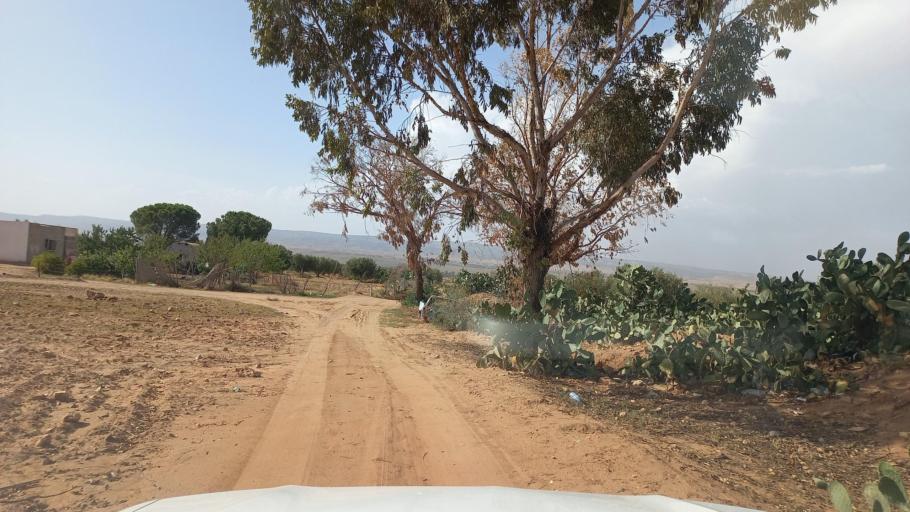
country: TN
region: Al Qasrayn
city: Kasserine
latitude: 35.2060
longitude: 8.9692
